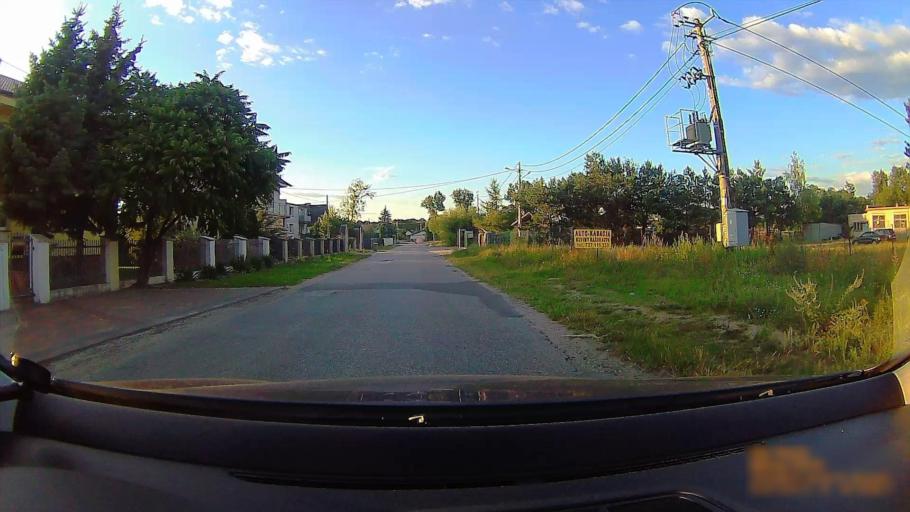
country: PL
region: Greater Poland Voivodeship
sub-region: Konin
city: Konin
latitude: 52.2133
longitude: 18.3252
